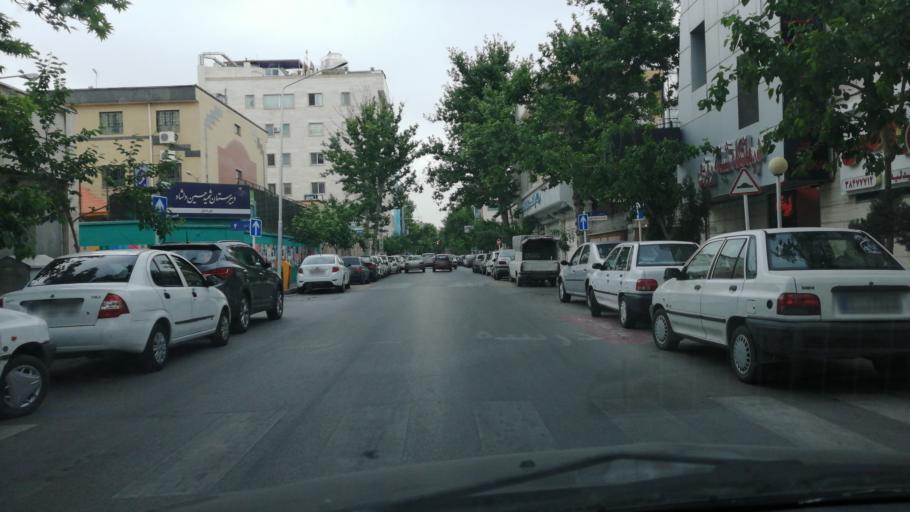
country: IR
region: Razavi Khorasan
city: Mashhad
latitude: 36.2944
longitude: 59.5812
